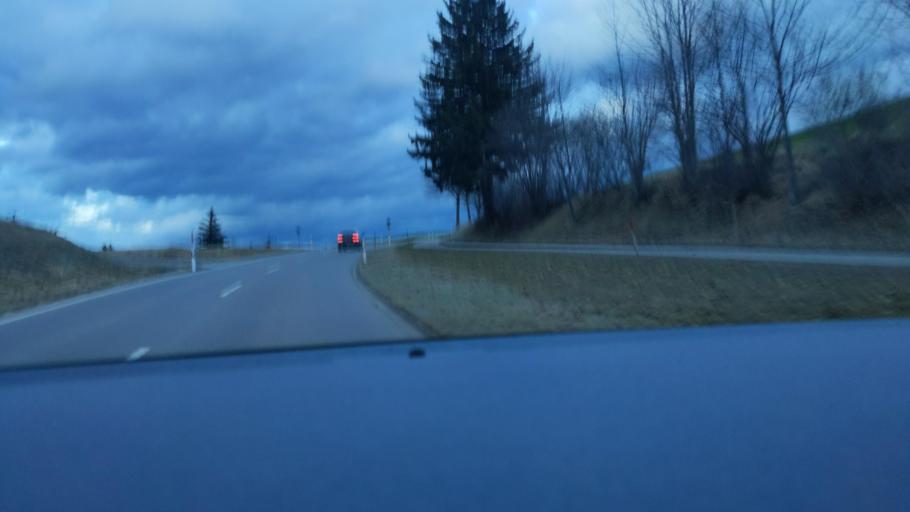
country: DE
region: Bavaria
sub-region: Swabia
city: Pfronten
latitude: 47.5880
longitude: 10.5689
